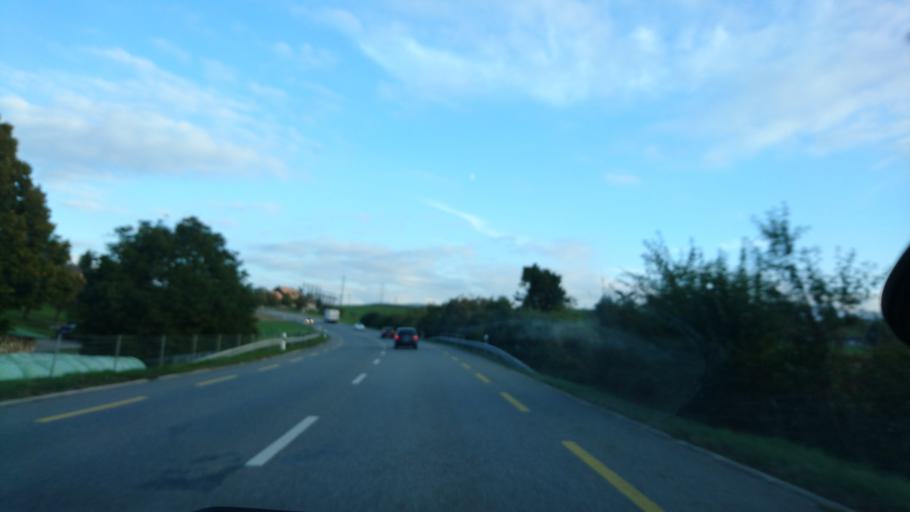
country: CH
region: Bern
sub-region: Bern-Mittelland District
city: Biglen
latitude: 46.9121
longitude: 7.6253
